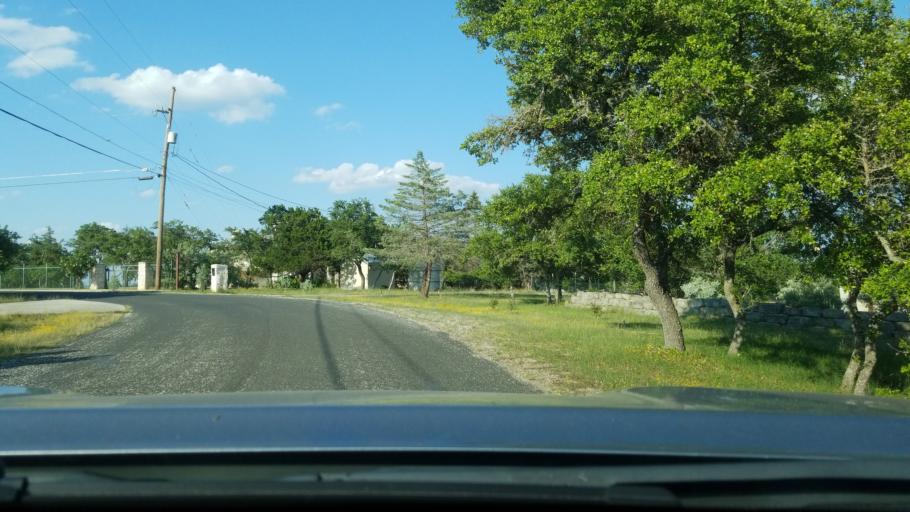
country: US
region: Texas
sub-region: Bexar County
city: Timberwood Park
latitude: 29.7063
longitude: -98.4442
